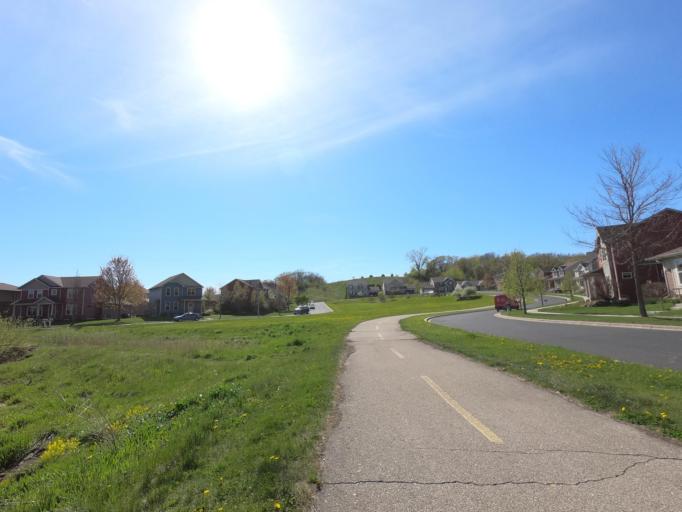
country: US
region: Wisconsin
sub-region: Dane County
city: Middleton
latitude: 43.1031
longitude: -89.5434
